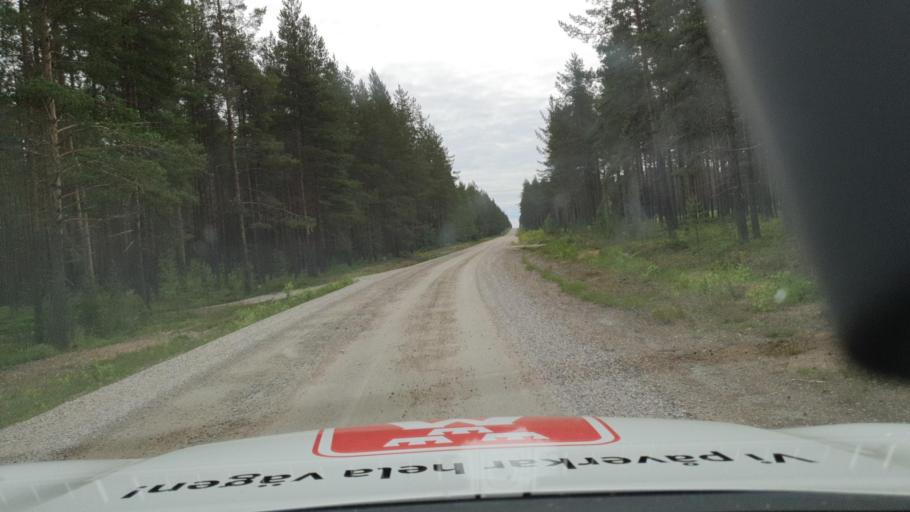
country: SE
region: Vaesterbotten
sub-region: Skelleftea Kommun
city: Forsbacka
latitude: 64.6541
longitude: 20.4408
